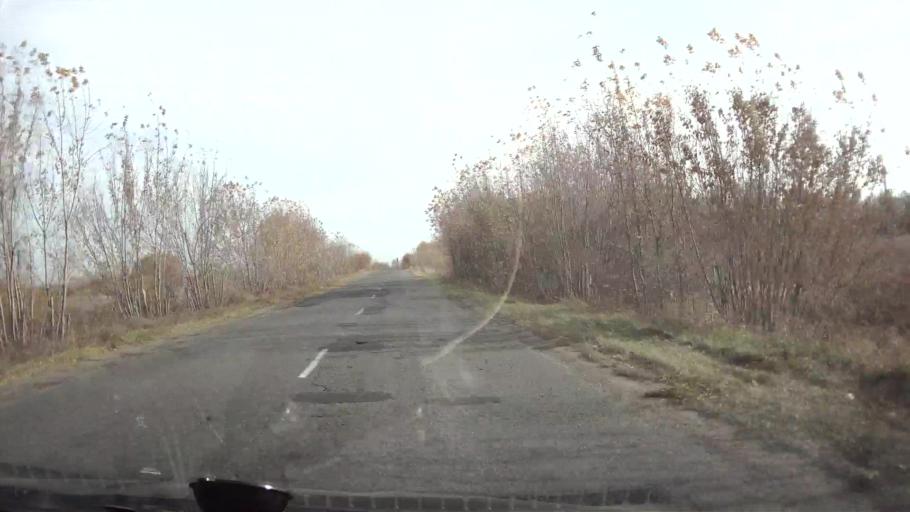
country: RU
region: Chuvashia
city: Alatyr'
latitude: 54.8447
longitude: 46.4644
